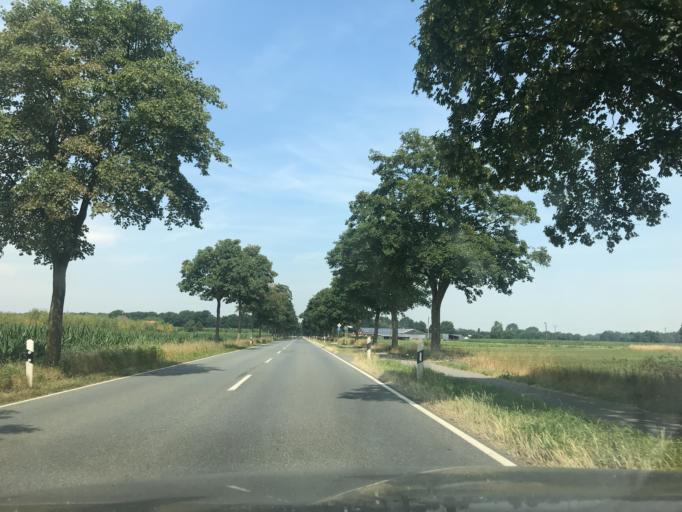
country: DE
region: North Rhine-Westphalia
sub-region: Regierungsbezirk Dusseldorf
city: Issum
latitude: 51.5100
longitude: 6.4202
